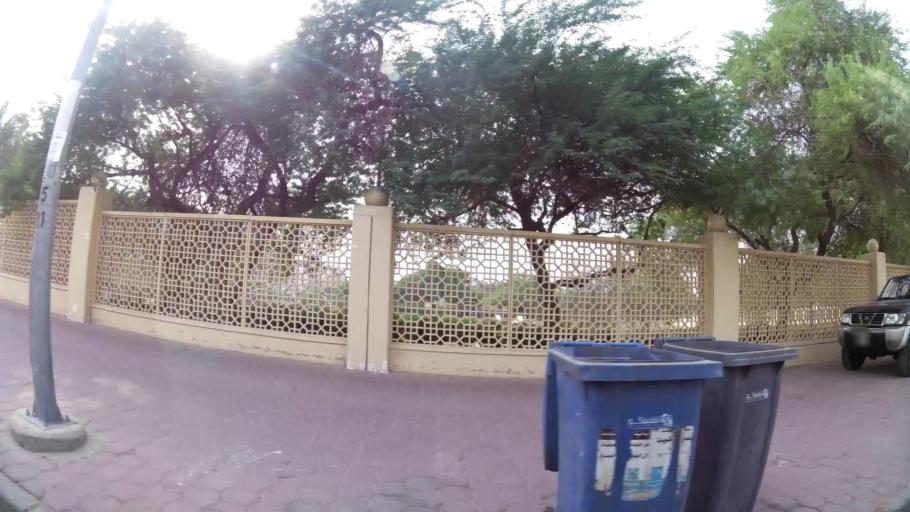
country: KW
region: Al Farwaniyah
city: Al Farwaniyah
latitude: 29.2906
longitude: 47.9631
